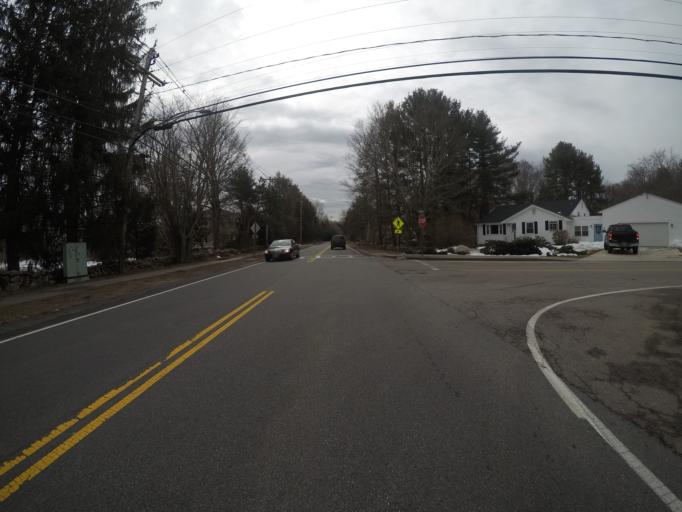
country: US
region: Massachusetts
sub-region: Bristol County
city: Easton
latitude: 42.0462
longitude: -71.1001
